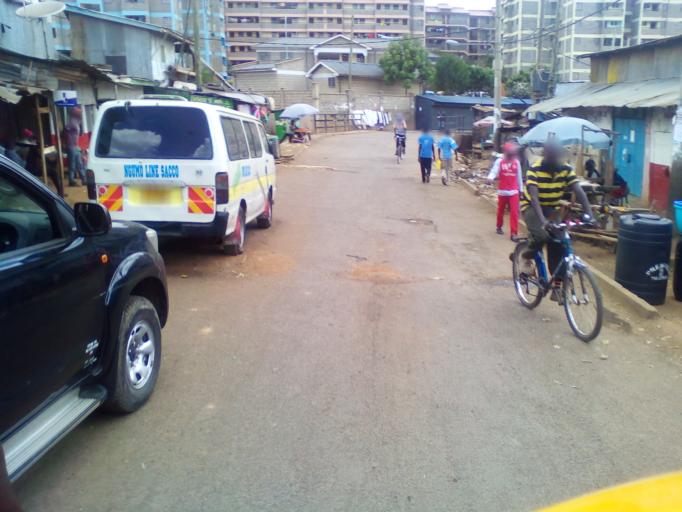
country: KE
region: Nairobi Area
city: Nairobi
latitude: -1.3149
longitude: 36.8002
